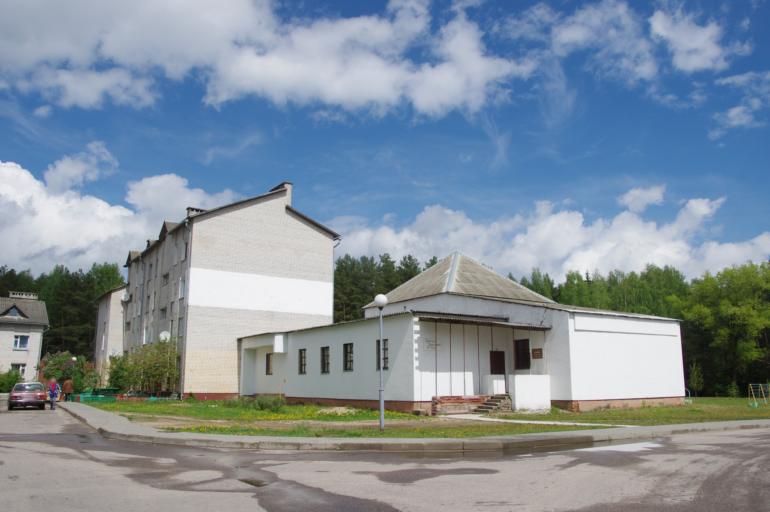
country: BY
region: Minsk
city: Narach
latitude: 54.9149
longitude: 26.7026
